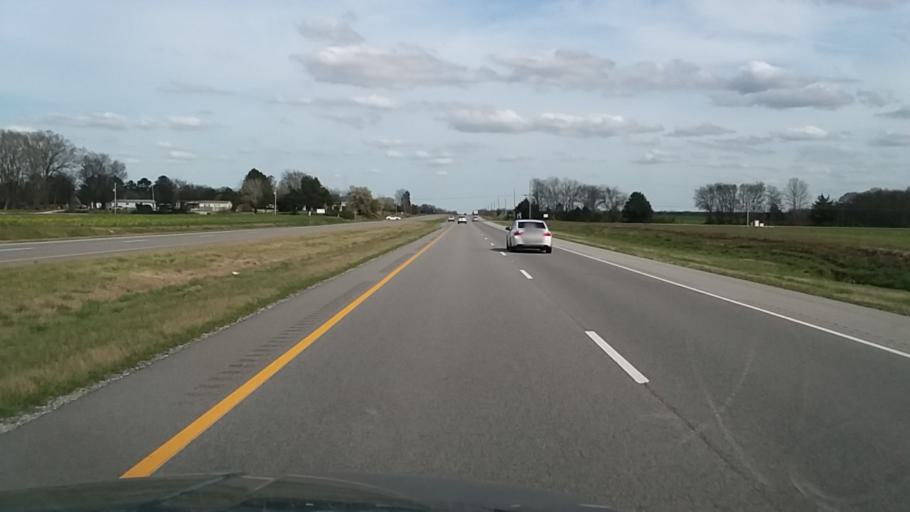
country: US
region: Alabama
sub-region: Colbert County
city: Muscle Shoals
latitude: 34.6847
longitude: -87.5670
